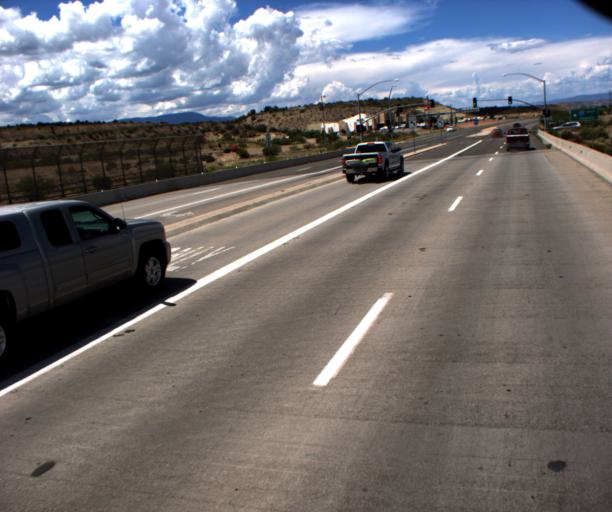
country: US
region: Arizona
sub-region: Yavapai County
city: Camp Verde
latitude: 34.5781
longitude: -111.8840
